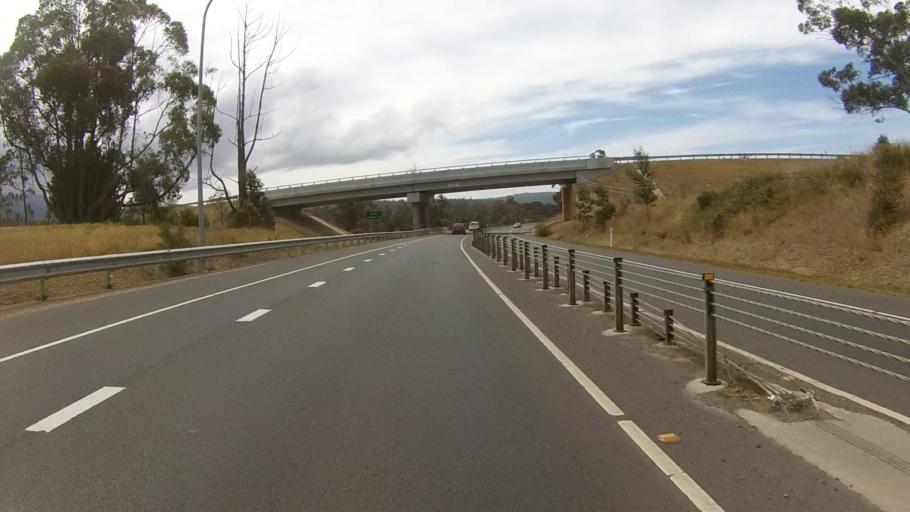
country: AU
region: Tasmania
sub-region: Kingborough
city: Kingston
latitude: -42.9839
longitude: 147.2894
